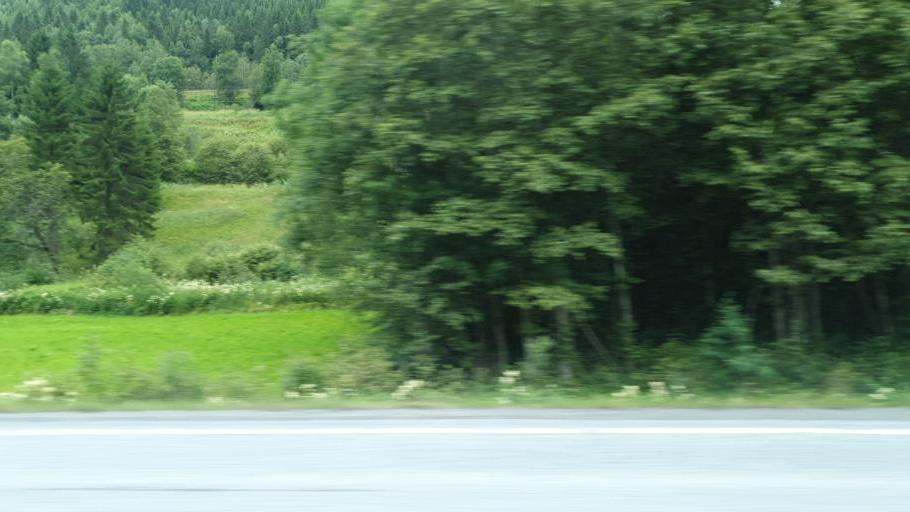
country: NO
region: Sor-Trondelag
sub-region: Midtre Gauldal
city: Storen
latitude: 63.0111
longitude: 10.2451
